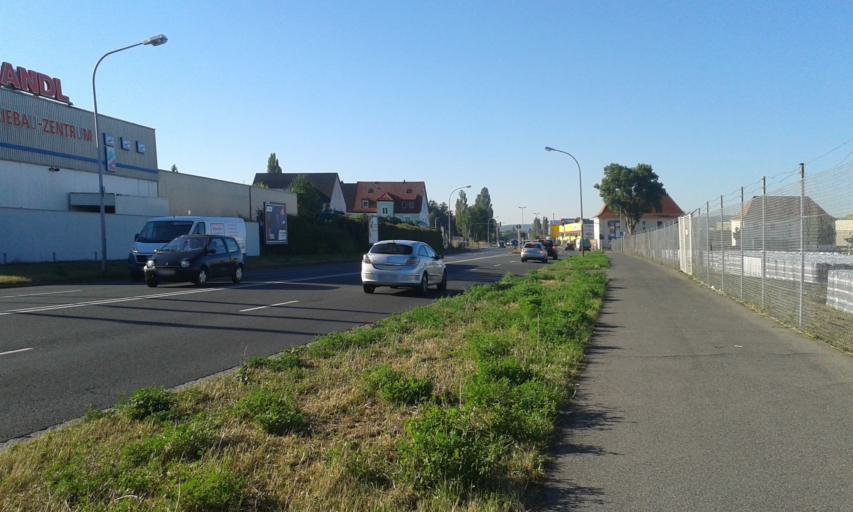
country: DE
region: Bavaria
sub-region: Upper Franconia
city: Bamberg
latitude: 49.8915
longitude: 10.9222
